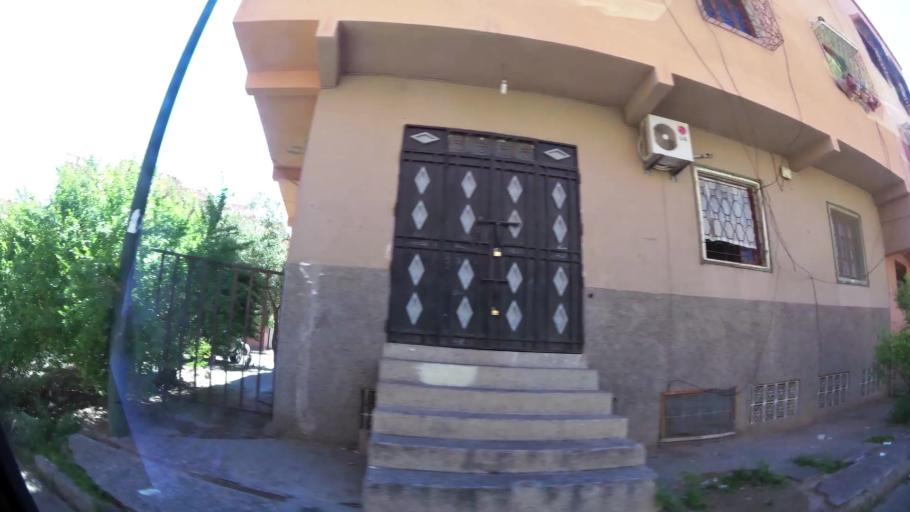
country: MA
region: Marrakech-Tensift-Al Haouz
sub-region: Marrakech
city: Marrakesh
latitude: 31.6588
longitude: -7.9904
